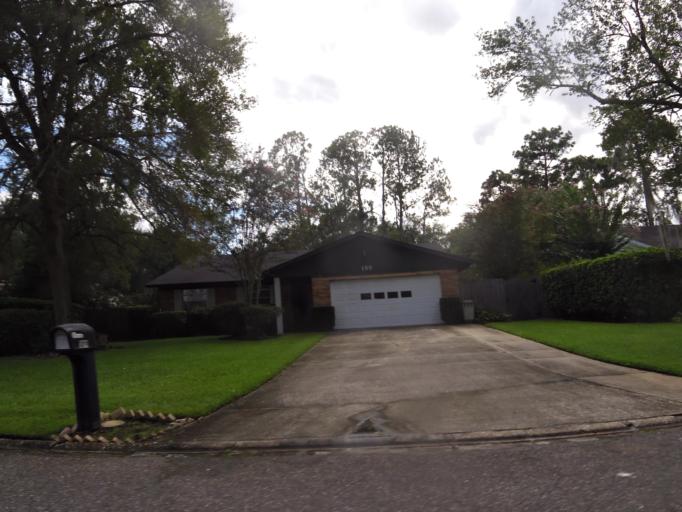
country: US
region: Florida
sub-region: Clay County
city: Lakeside
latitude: 30.1292
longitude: -81.7679
